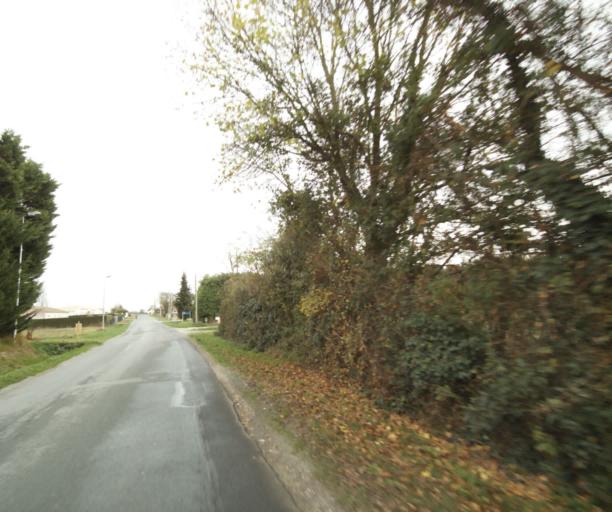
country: FR
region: Poitou-Charentes
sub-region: Departement de la Charente-Maritime
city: Corme-Royal
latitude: 45.7444
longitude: -0.8084
